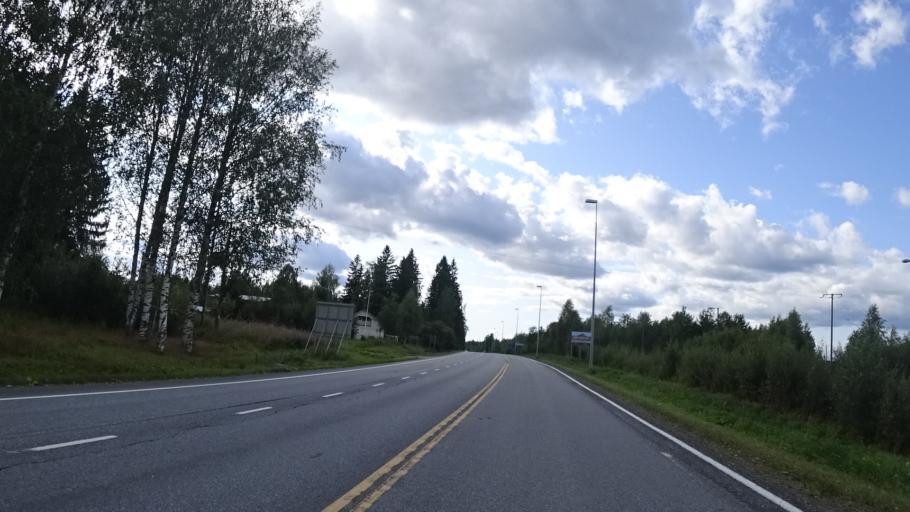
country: RU
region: Republic of Karelia
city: Vyartsilya
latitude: 62.1764
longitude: 30.5878
